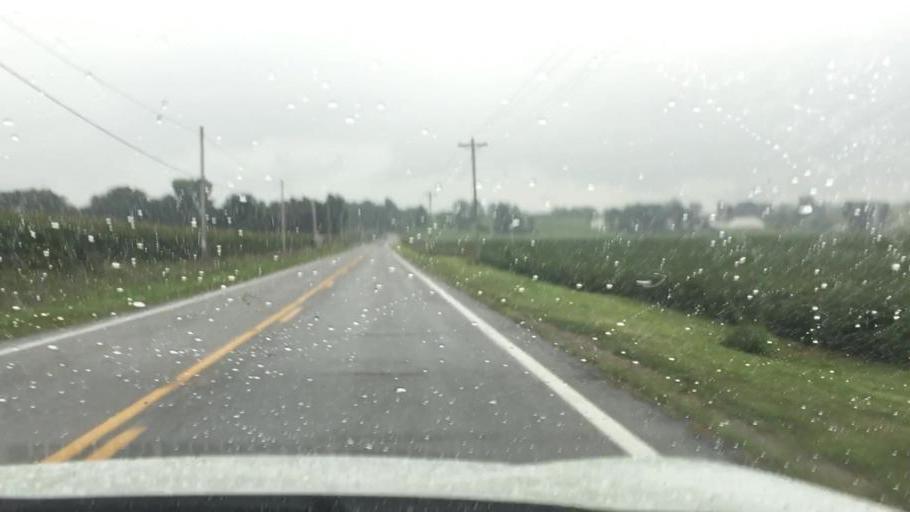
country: US
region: Ohio
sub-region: Champaign County
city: Mechanicsburg
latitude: 40.0268
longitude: -83.6399
